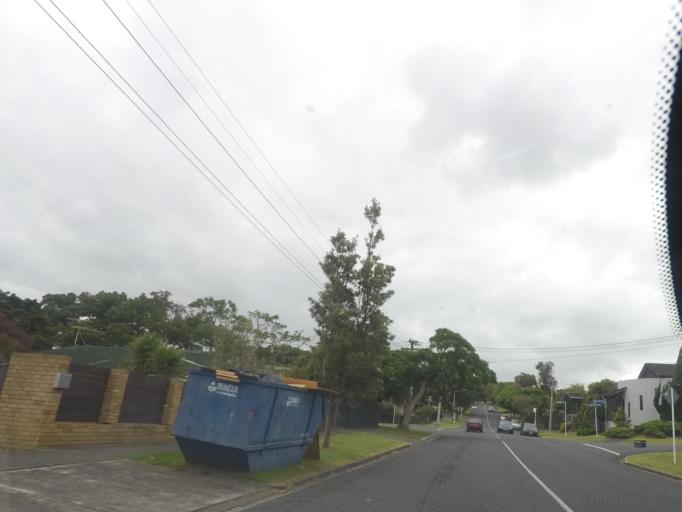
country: NZ
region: Auckland
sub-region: Auckland
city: Tamaki
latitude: -36.8655
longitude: 174.8581
